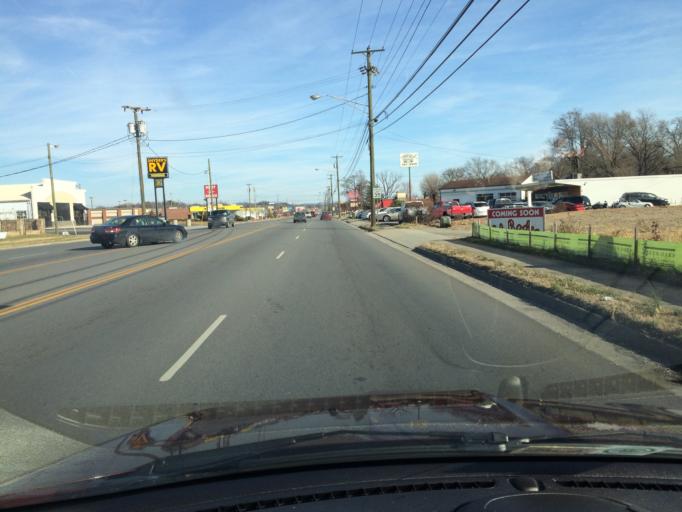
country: US
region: Virginia
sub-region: City of Salem
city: Salem
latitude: 37.2877
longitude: -80.0940
